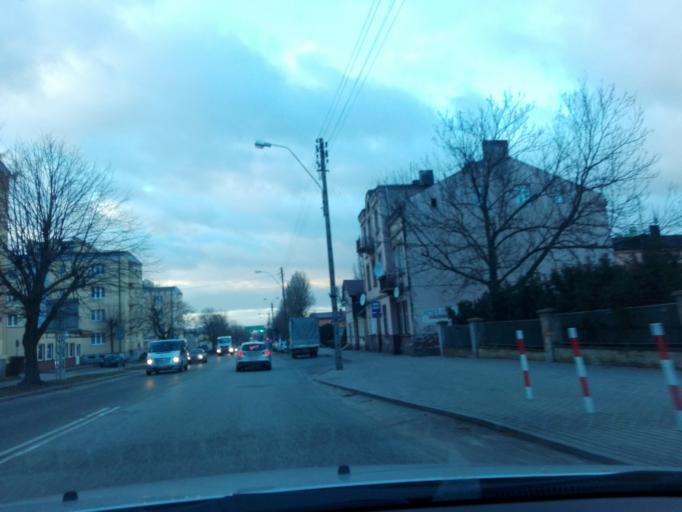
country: PL
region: Lodz Voivodeship
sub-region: Powiat kutnowski
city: Kutno
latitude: 52.2336
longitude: 19.3568
